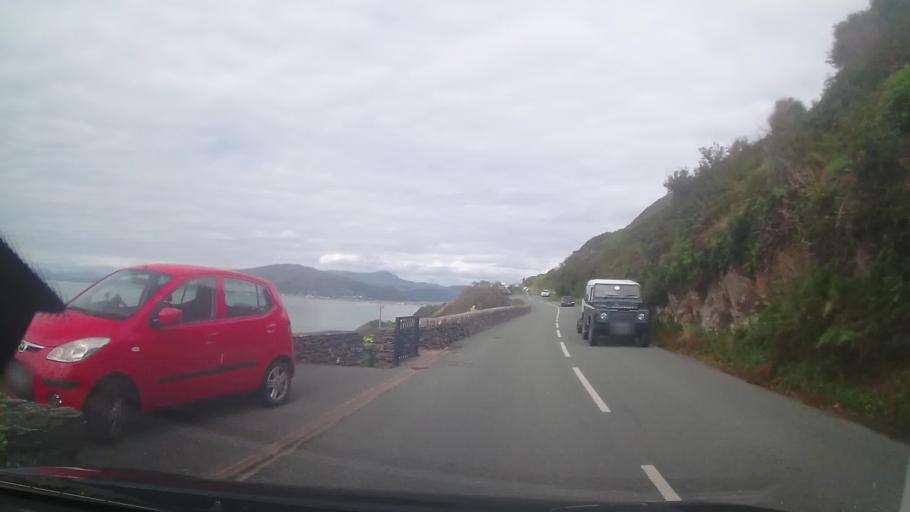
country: GB
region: Wales
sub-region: Gwynedd
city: Barmouth
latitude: 52.6775
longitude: -4.0738
